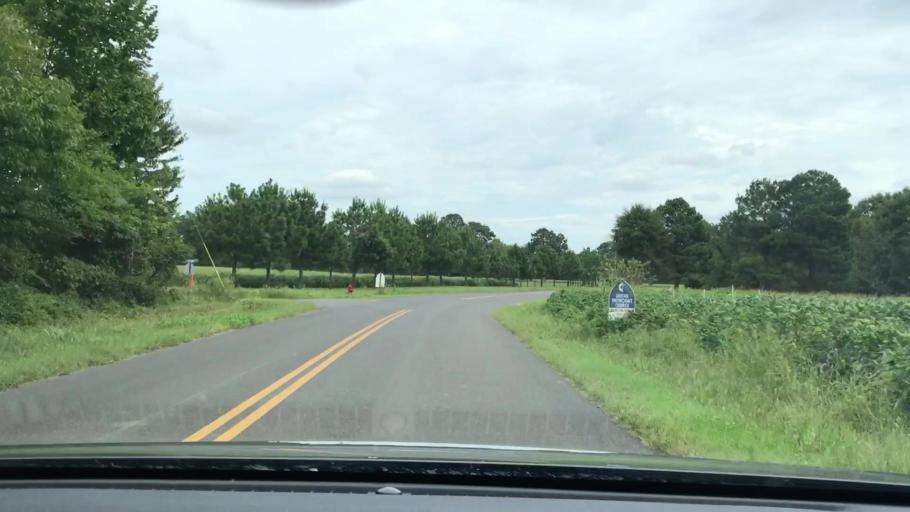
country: US
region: Kentucky
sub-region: Marshall County
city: Benton
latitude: 36.8322
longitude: -88.3719
